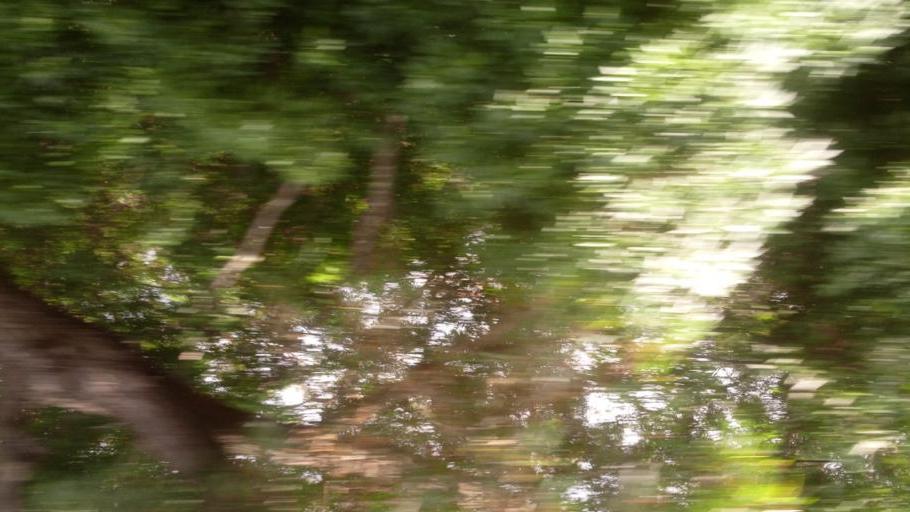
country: AU
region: New South Wales
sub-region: Blue Mountains Municipality
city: Hazelbrook
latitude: -33.7356
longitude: 150.4795
